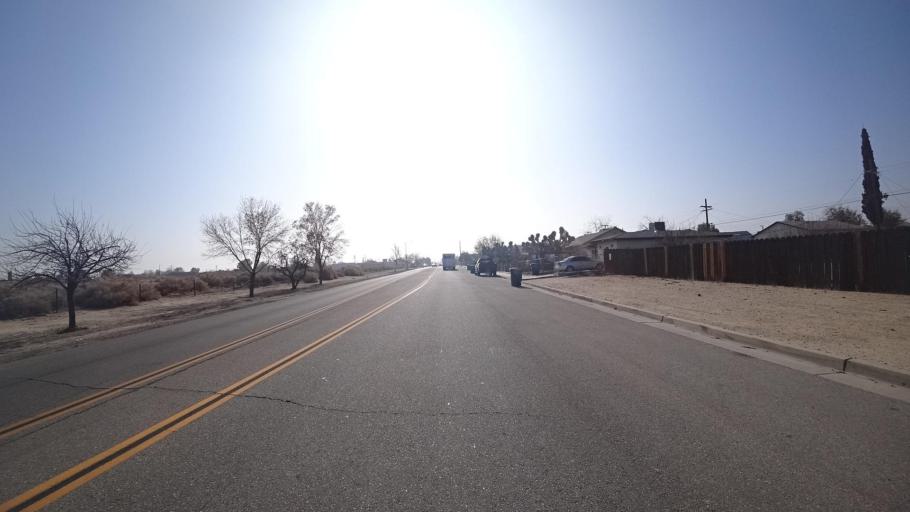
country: US
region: California
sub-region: Kern County
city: Ford City
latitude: 35.1602
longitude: -119.4564
